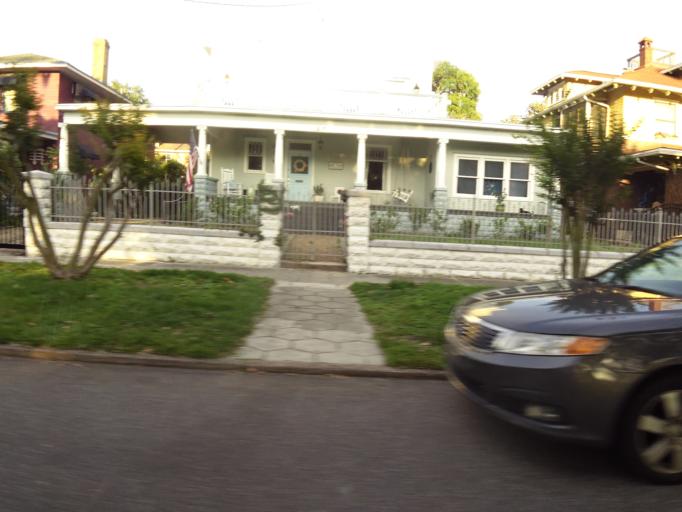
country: US
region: Florida
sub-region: Duval County
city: Jacksonville
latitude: 30.3385
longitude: -81.6574
